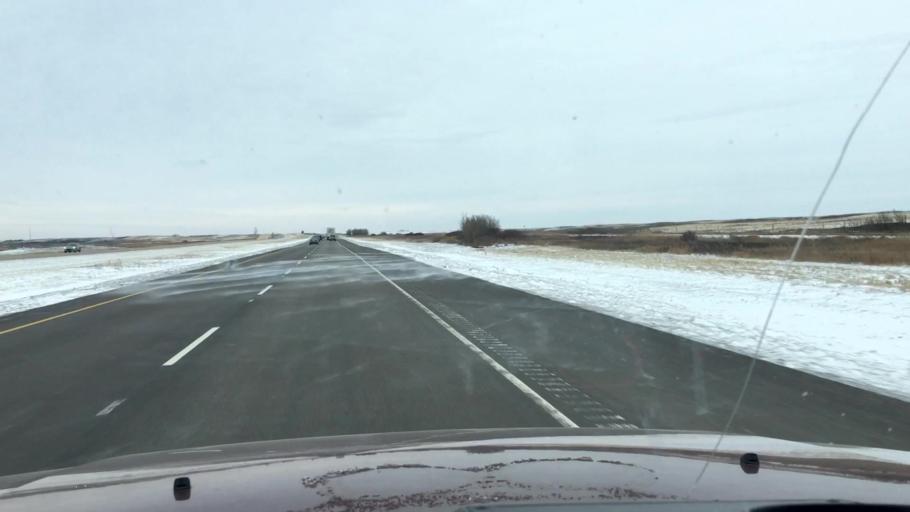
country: CA
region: Saskatchewan
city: Moose Jaw
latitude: 50.8908
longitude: -105.6260
